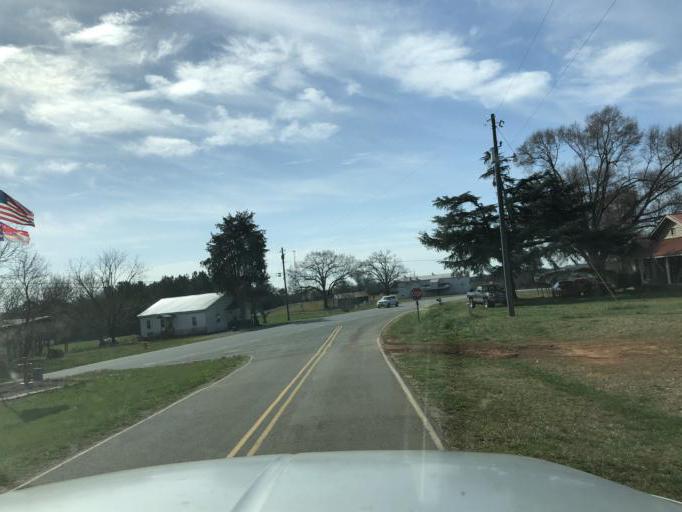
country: US
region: North Carolina
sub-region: Cleveland County
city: Shelby
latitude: 35.4690
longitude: -81.6334
